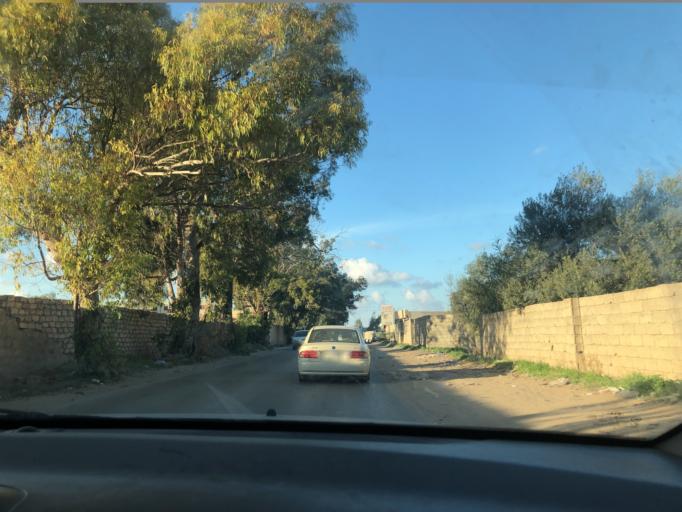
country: LY
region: Tripoli
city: Tagiura
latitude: 32.8620
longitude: 13.2785
